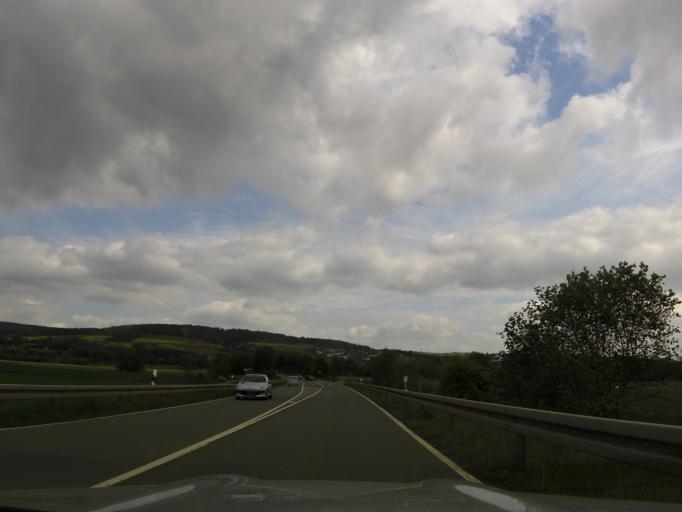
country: DE
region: Hesse
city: Burgsolms
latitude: 50.5471
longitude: 8.4092
